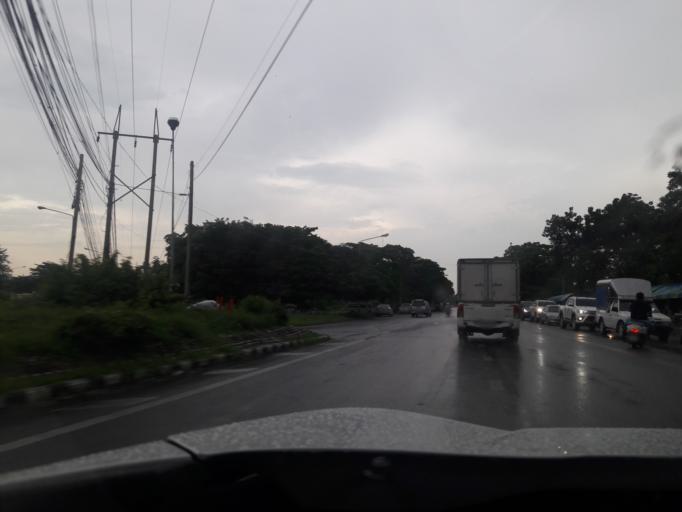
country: TH
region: Lop Buri
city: Lop Buri
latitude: 14.8061
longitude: 100.6349
